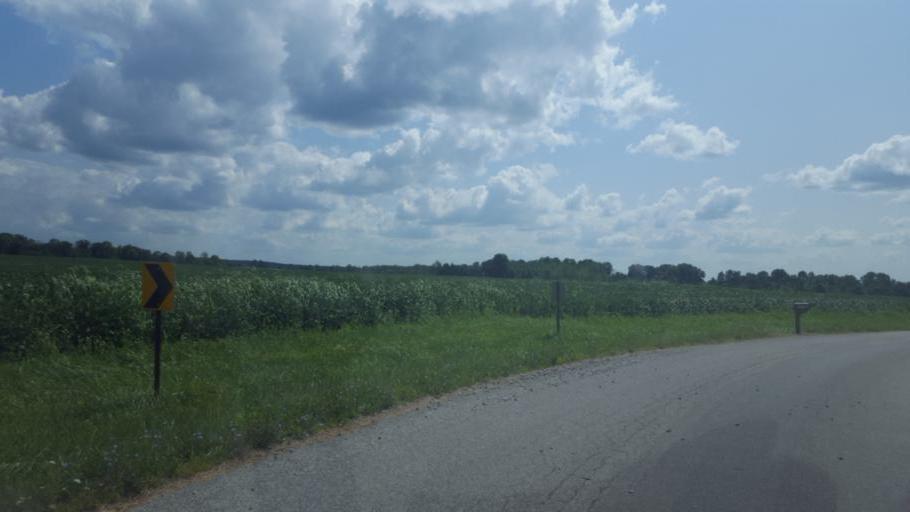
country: US
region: Ohio
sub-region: Delaware County
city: Sunbury
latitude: 40.3322
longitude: -82.8581
